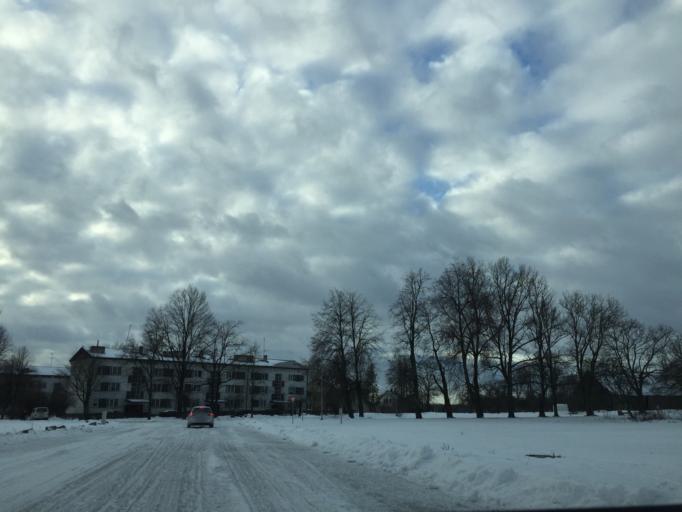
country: LV
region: Lielvarde
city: Lielvarde
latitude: 56.6320
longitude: 24.7529
